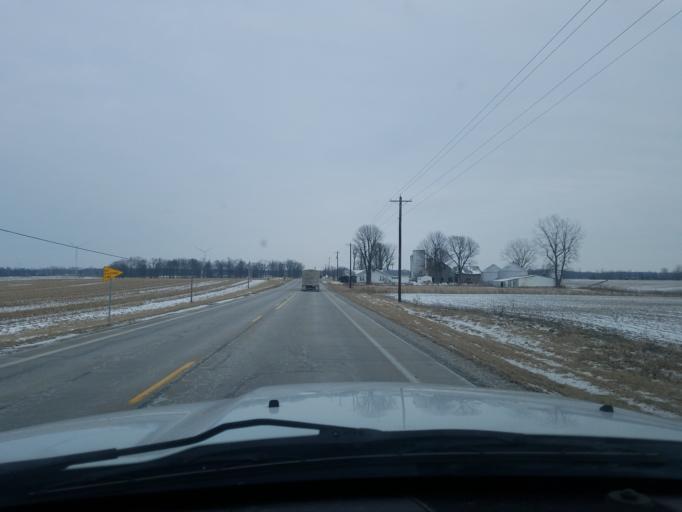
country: US
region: Indiana
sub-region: Randolph County
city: Lynn
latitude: 40.0486
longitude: -84.9862
